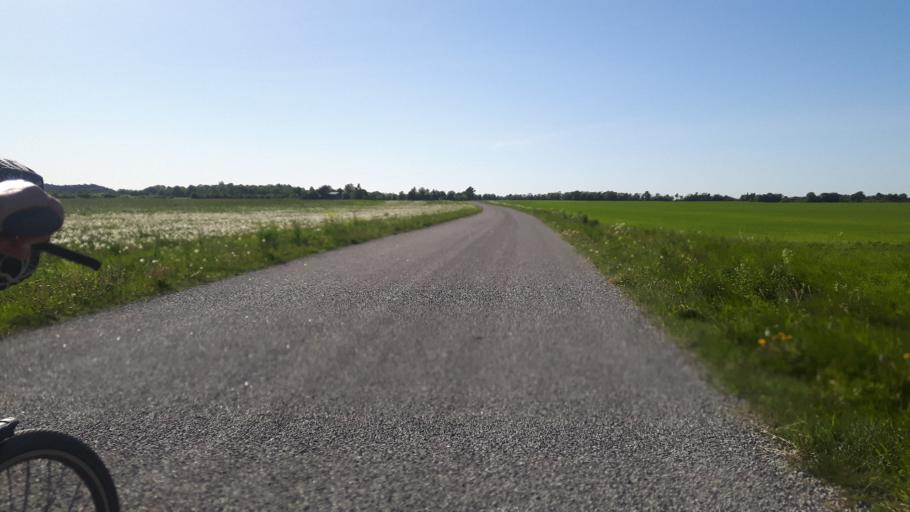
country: EE
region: Ida-Virumaa
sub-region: Kohtla-Jaerve linn
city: Kohtla-Jarve
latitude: 59.4336
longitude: 27.2092
